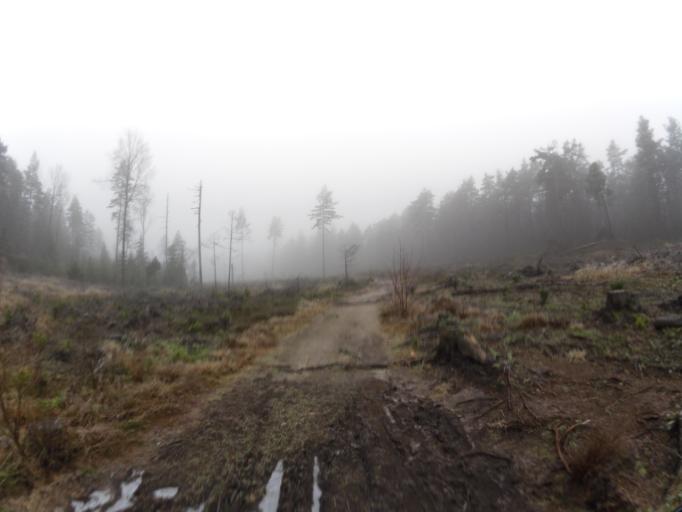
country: NO
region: Ostfold
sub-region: Fredrikstad
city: Fredrikstad
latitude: 59.2621
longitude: 10.9824
